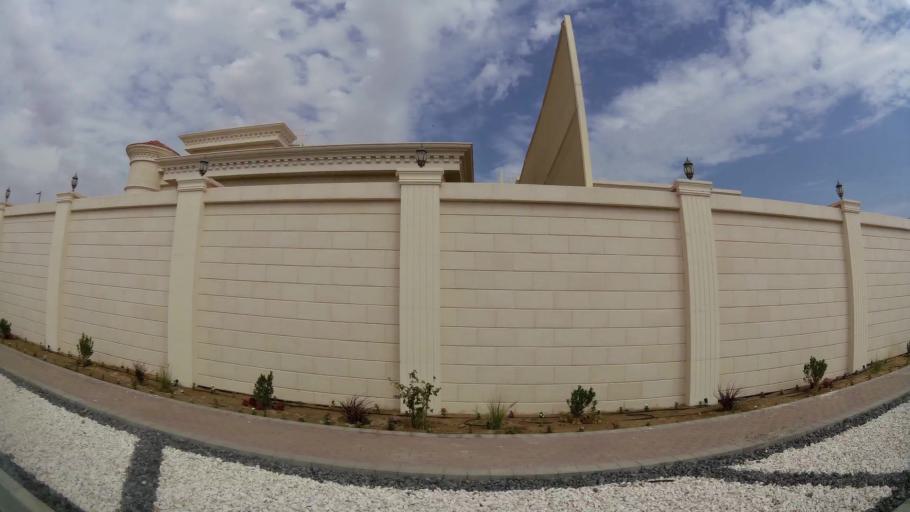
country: AE
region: Abu Dhabi
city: Al Ain
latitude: 24.1881
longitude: 55.8069
